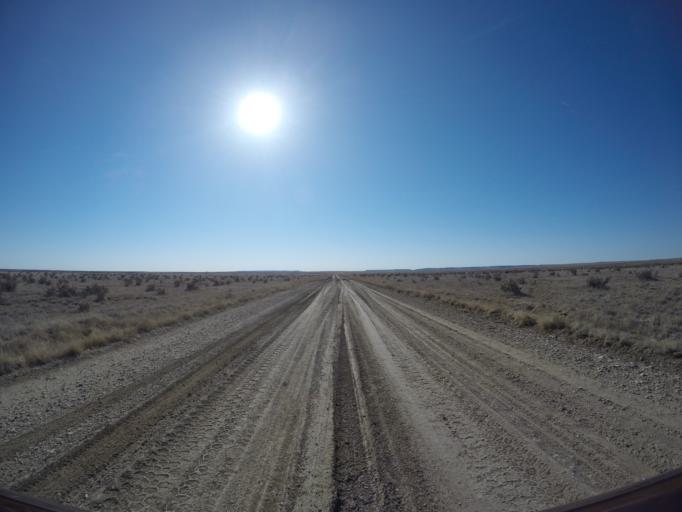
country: US
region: Colorado
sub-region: Otero County
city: La Junta
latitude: 37.7239
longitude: -103.6205
